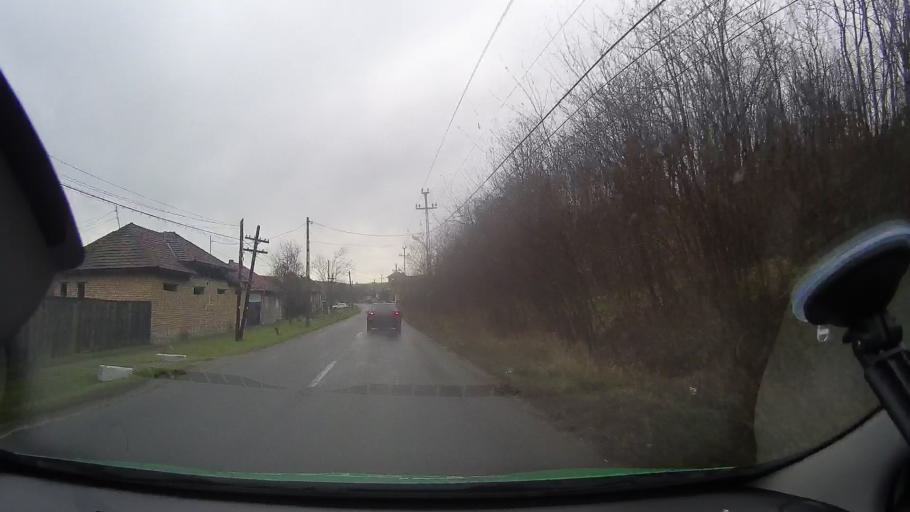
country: RO
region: Arad
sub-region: Comuna Sebis
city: Sebis
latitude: 46.3806
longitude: 22.1363
